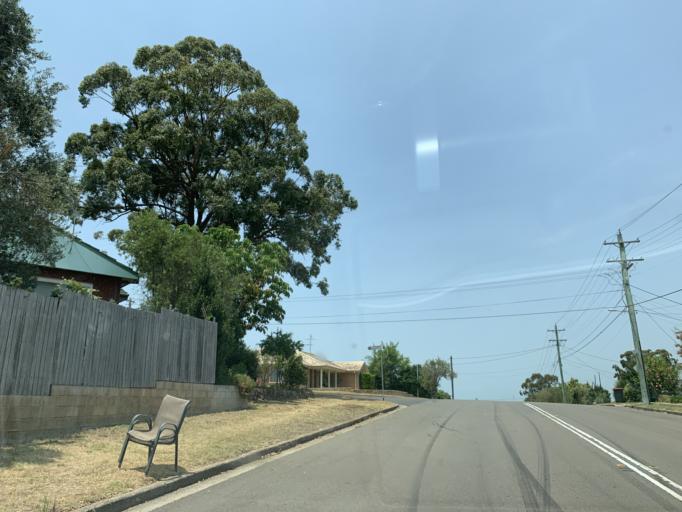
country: AU
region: New South Wales
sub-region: Blacktown
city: Doonside
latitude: -33.7785
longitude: 150.8827
